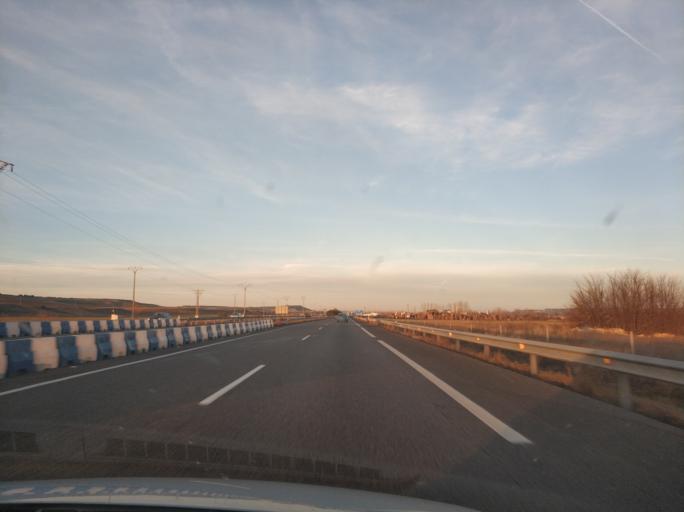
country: ES
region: Castille and Leon
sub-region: Provincia de Valladolid
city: Cubillas de Santa Marta
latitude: 41.8212
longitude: -4.5780
